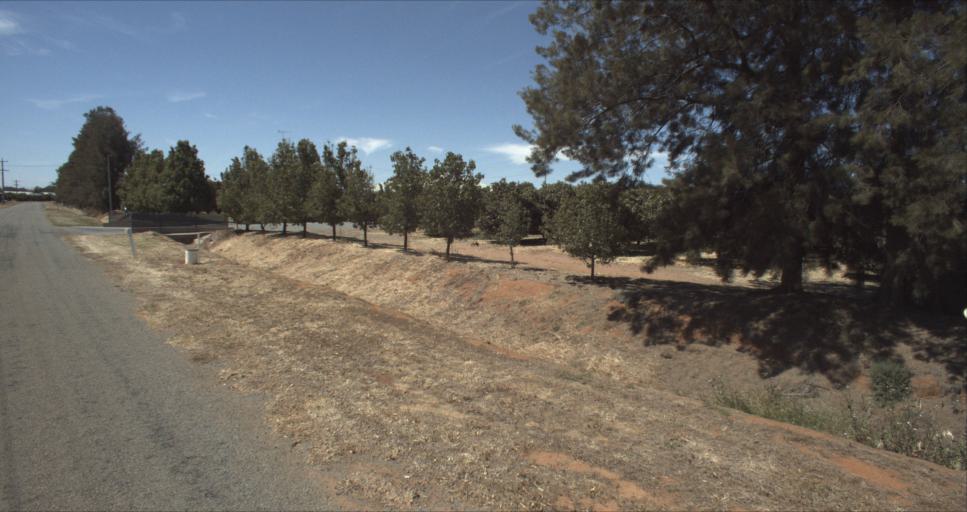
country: AU
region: New South Wales
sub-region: Leeton
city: Leeton
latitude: -34.6028
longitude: 146.4343
